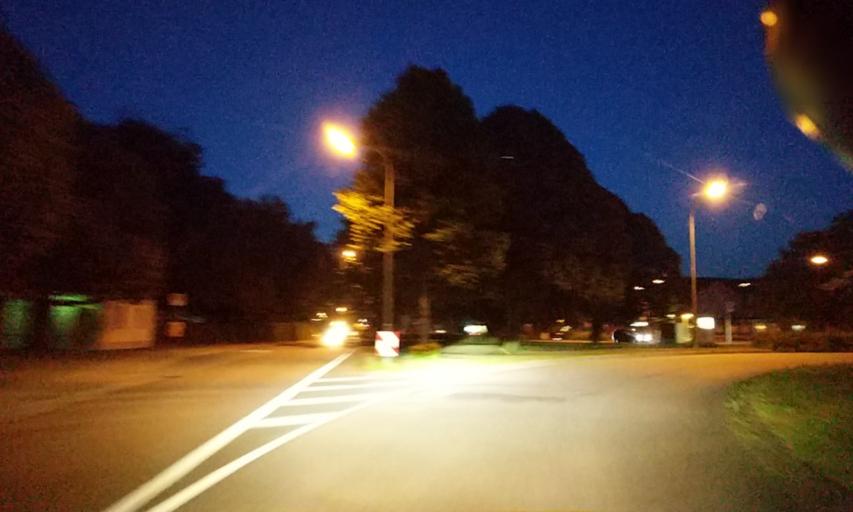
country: DE
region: Rheinland-Pfalz
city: Kaiserslautern
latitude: 49.4479
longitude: 7.7533
